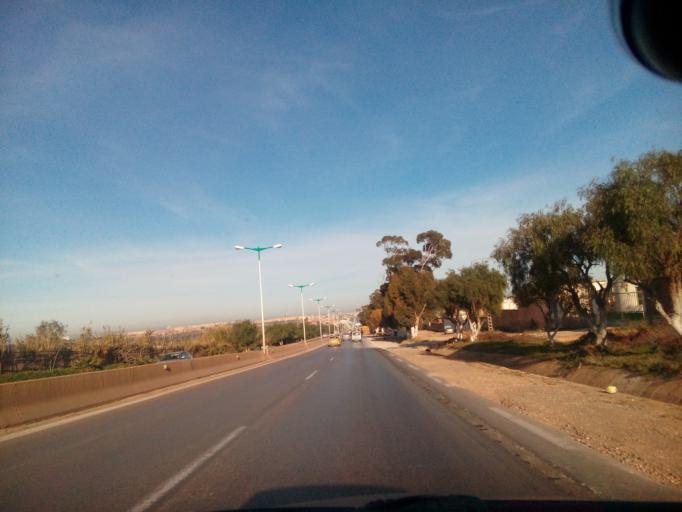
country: DZ
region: Mostaganem
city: Mostaganem
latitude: 35.8956
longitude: 0.1266
